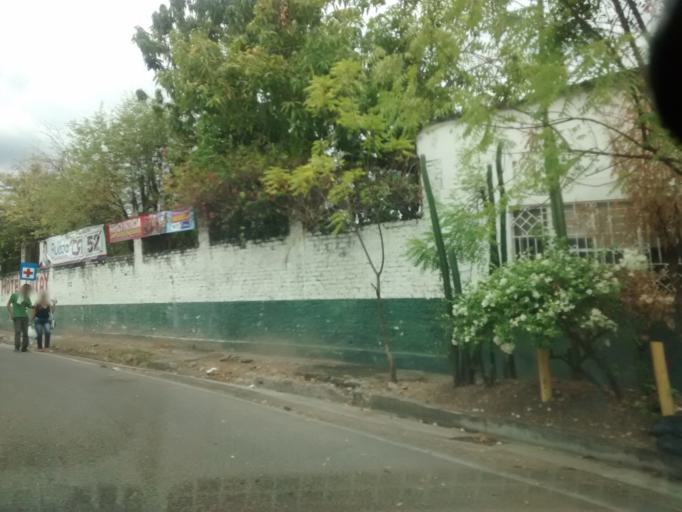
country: CO
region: Cundinamarca
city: Tocaima
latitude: 4.4561
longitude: -74.6359
